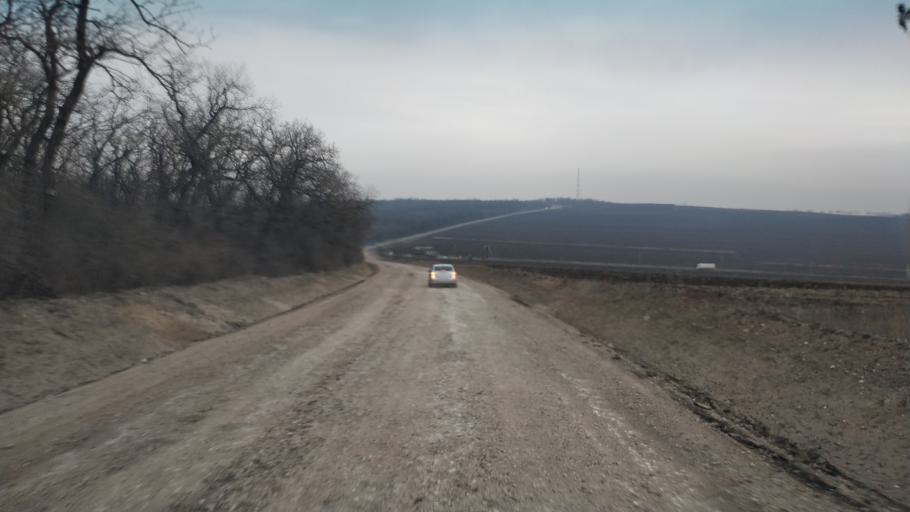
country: MD
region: Chisinau
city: Singera
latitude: 46.8537
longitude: 29.0167
